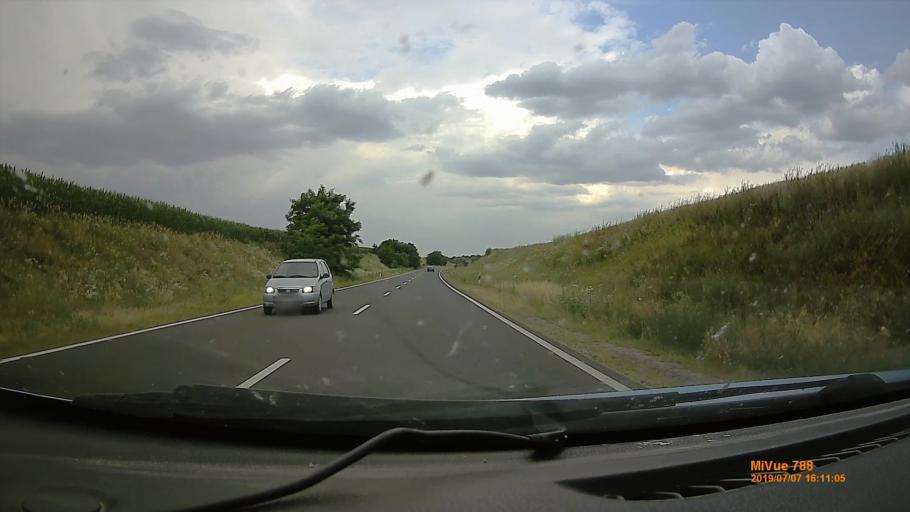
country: HU
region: Heves
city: Hatvan
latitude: 47.6723
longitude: 19.7175
